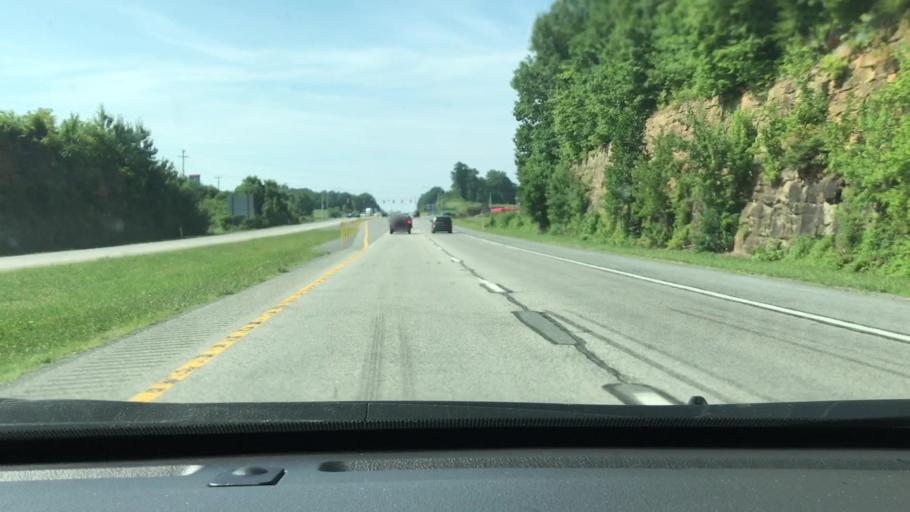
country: US
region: West Virginia
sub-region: Fayette County
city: Fayetteville
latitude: 38.0350
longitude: -81.1230
